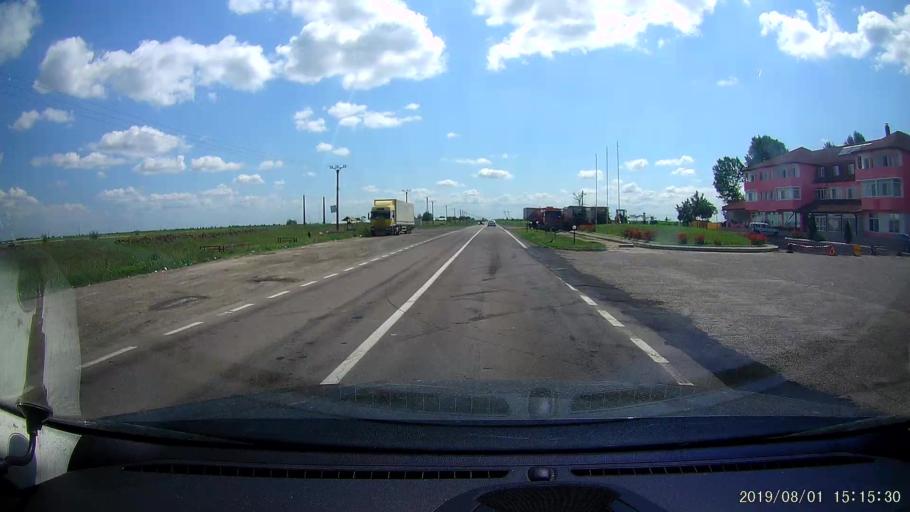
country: RO
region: Braila
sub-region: Comuna Tichilesti
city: Tichilesti
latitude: 45.1630
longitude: 27.8671
